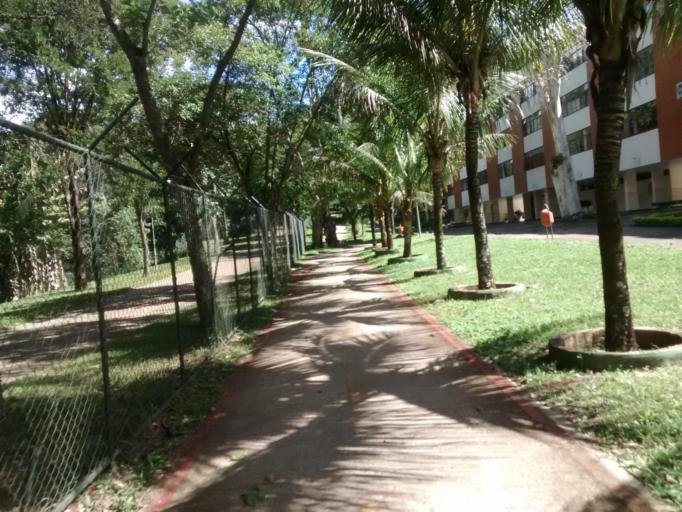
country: BR
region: Federal District
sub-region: Brasilia
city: Brasilia
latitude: -15.7405
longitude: -47.8844
